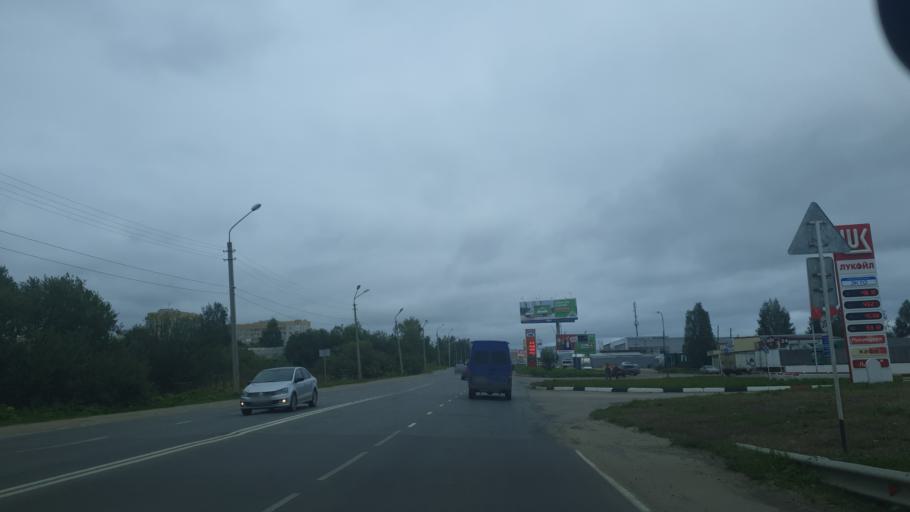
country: RU
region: Komi Republic
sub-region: Syktyvdinskiy Rayon
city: Syktyvkar
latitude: 61.6357
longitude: 50.8120
